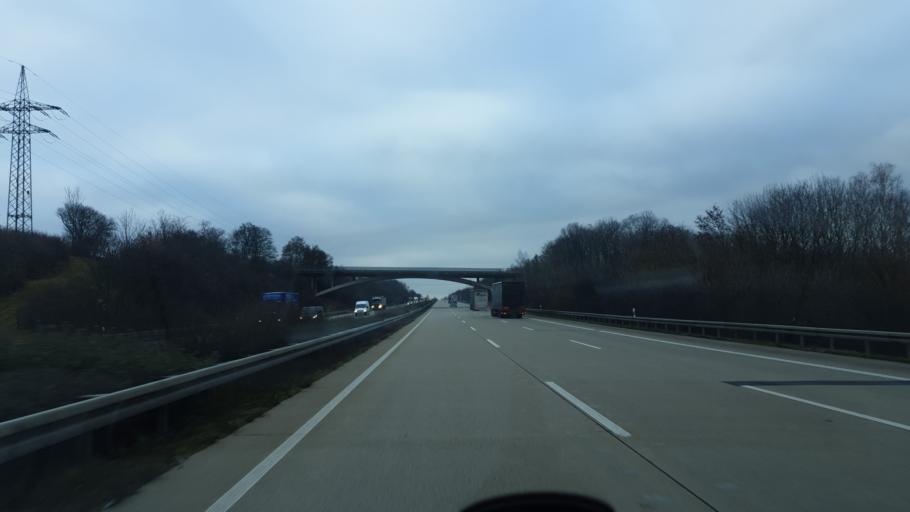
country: DE
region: Thuringia
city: Gosen
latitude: 50.9819
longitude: 11.8833
